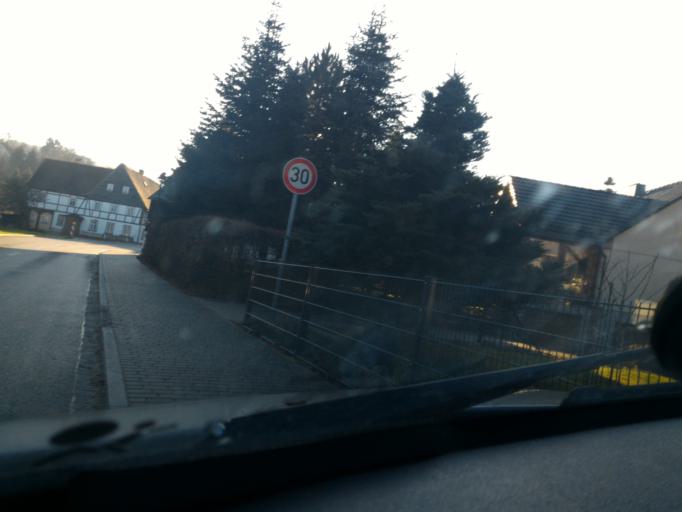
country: DE
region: Saxony
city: Kurort Jonsdorf
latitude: 50.8560
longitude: 14.6928
